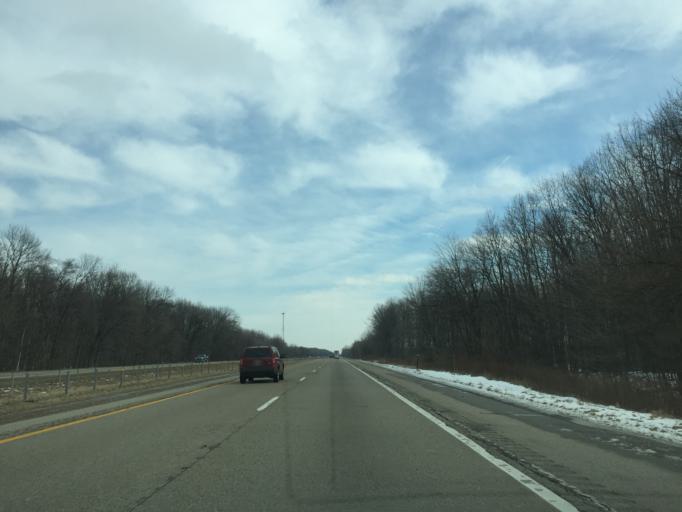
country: US
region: Michigan
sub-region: Ionia County
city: Saranac
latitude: 42.8792
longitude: -85.1851
